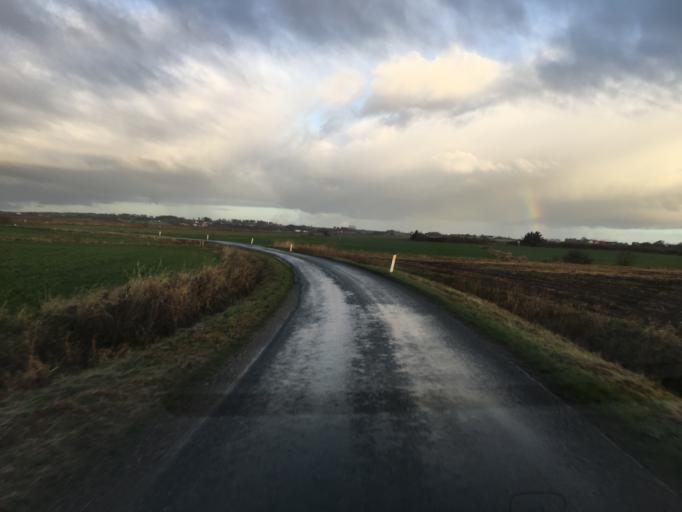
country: DK
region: South Denmark
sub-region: Tonder Kommune
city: Sherrebek
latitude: 55.1410
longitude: 8.8268
